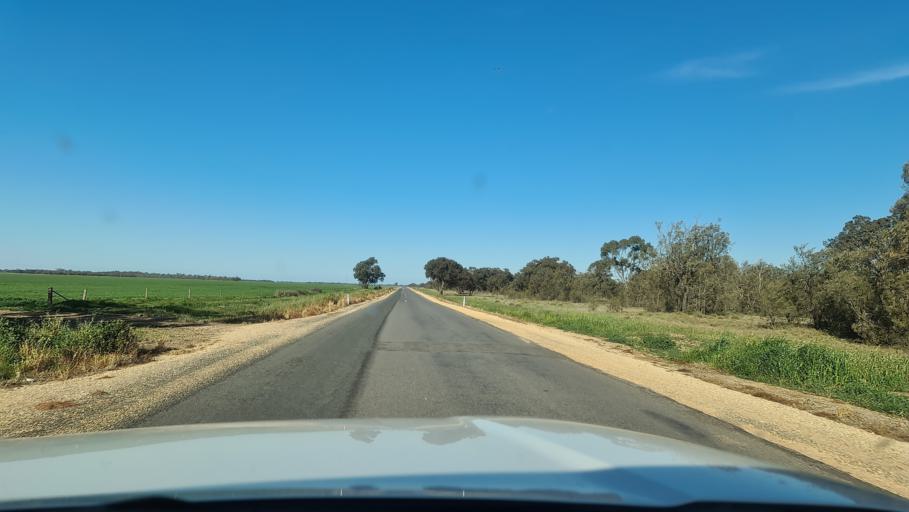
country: AU
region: Victoria
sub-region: Horsham
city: Horsham
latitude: -36.4492
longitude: 142.5400
